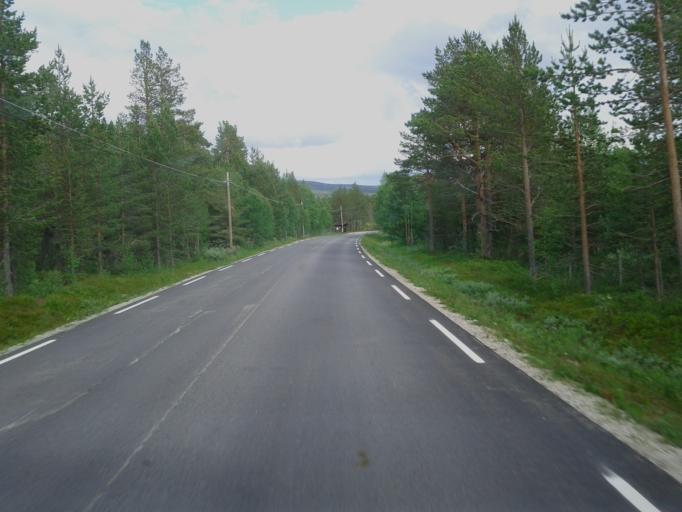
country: NO
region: Sor-Trondelag
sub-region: Roros
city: Roros
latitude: 62.3040
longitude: 11.7139
